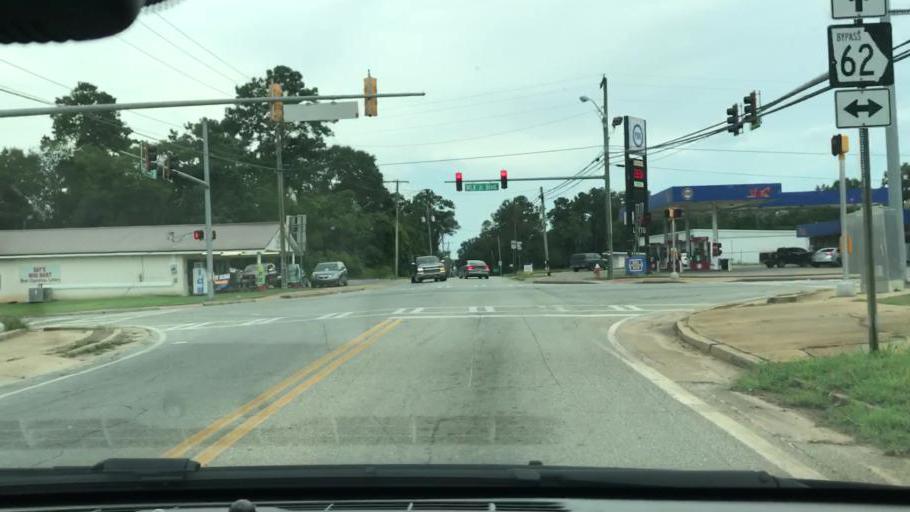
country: US
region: Georgia
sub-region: Early County
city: Blakely
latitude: 31.3919
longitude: -84.9333
